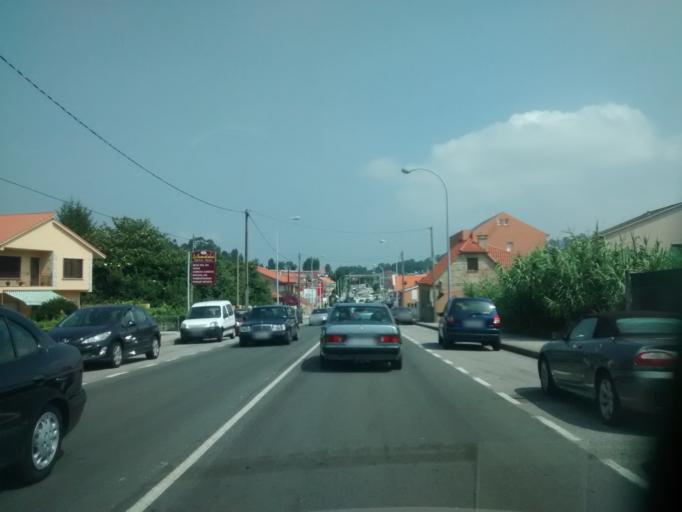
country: ES
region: Galicia
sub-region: Provincia de Pontevedra
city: Sanxenxo
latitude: 42.4095
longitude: -8.8130
